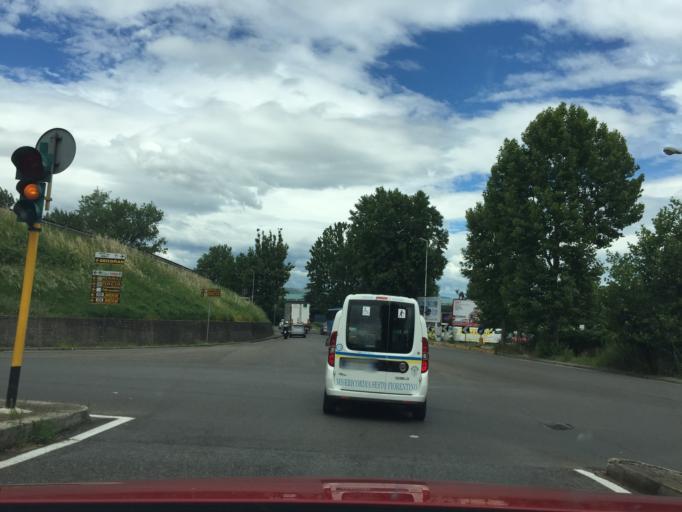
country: IT
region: Tuscany
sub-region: Province of Florence
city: Sesto Fiorentino
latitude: 43.7988
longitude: 11.2043
